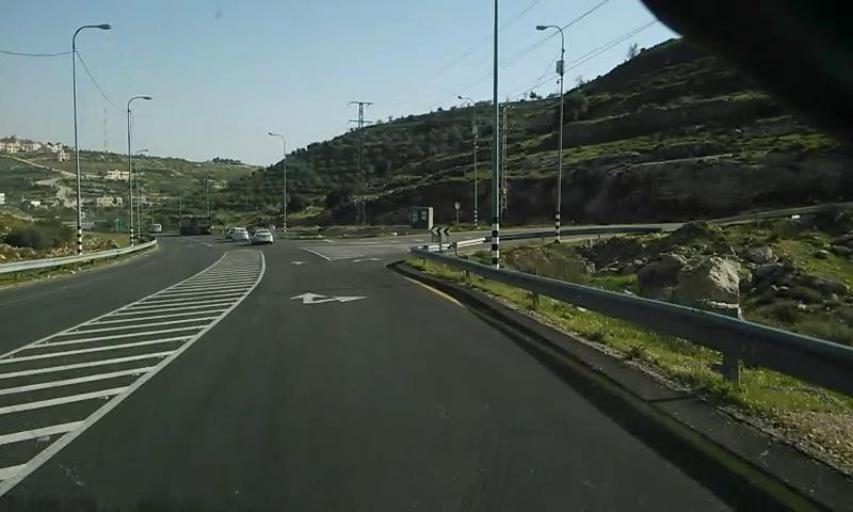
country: PS
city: Al Buq`ah
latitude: 31.5182
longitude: 35.1336
